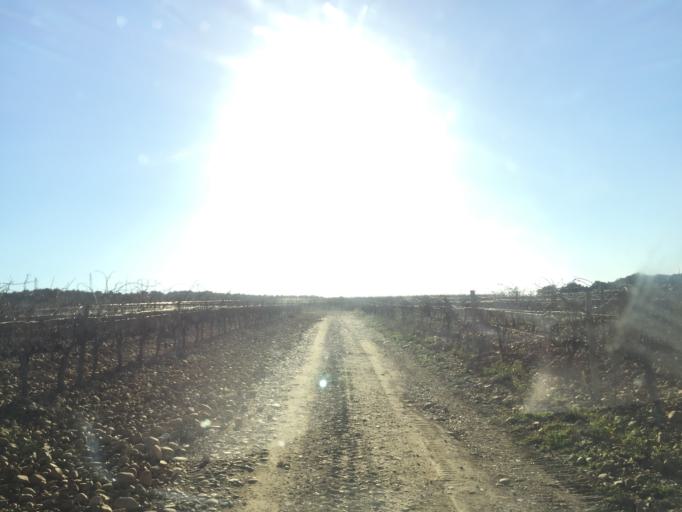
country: FR
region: Provence-Alpes-Cote d'Azur
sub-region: Departement du Vaucluse
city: Bedarrides
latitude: 44.0270
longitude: 4.8913
